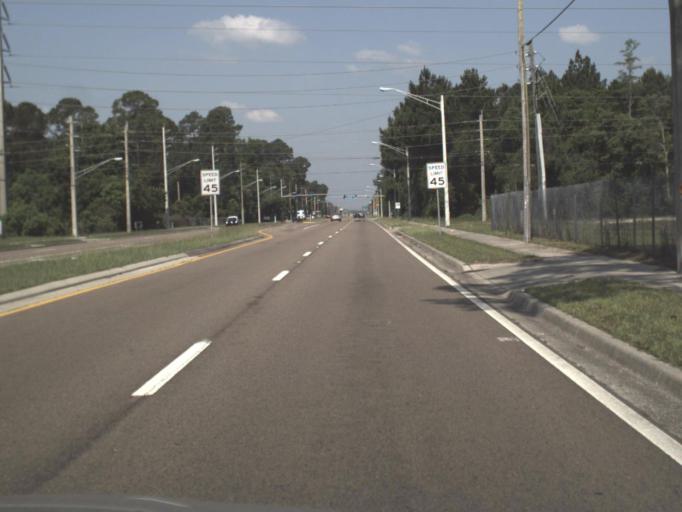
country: US
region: Florida
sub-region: Clay County
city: Bellair-Meadowbrook Terrace
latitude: 30.2473
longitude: -81.8328
